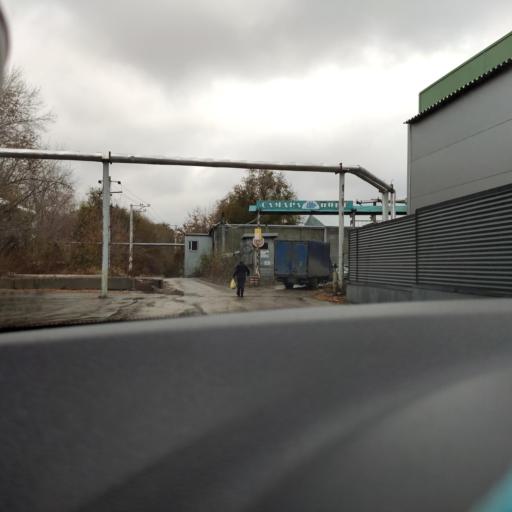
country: RU
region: Samara
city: Petra-Dubrava
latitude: 53.2545
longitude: 50.2979
